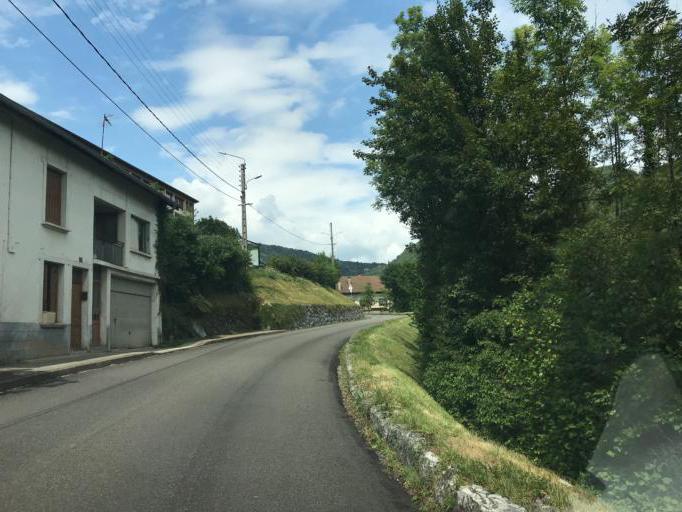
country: FR
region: Franche-Comte
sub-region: Departement du Jura
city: Saint-Claude
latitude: 46.4033
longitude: 5.8656
